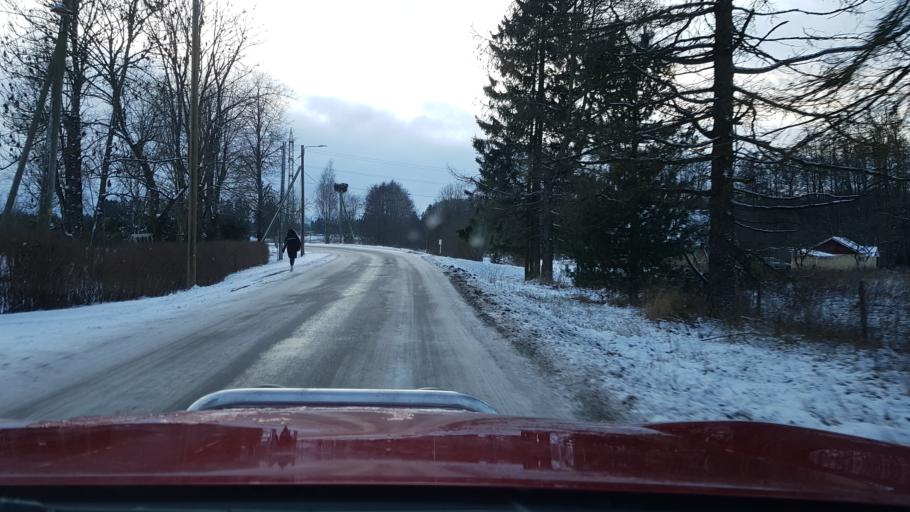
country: EE
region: Harju
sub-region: Maardu linn
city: Maardu
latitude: 59.4269
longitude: 25.0189
